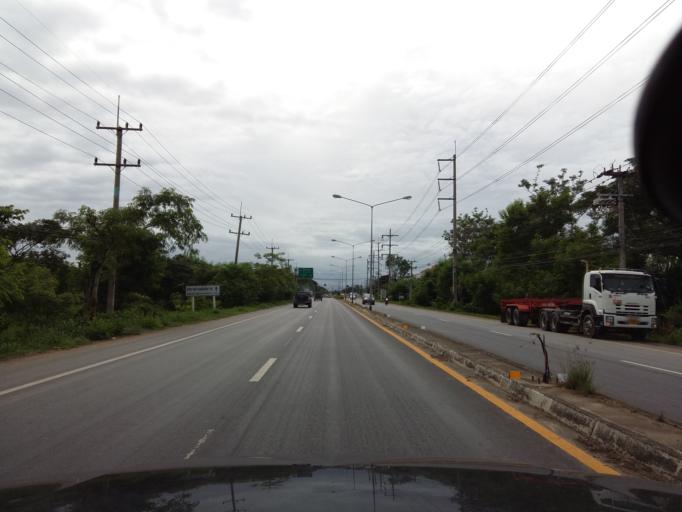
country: TH
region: Chiang Mai
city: Hang Dong
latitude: 18.7232
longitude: 98.9421
